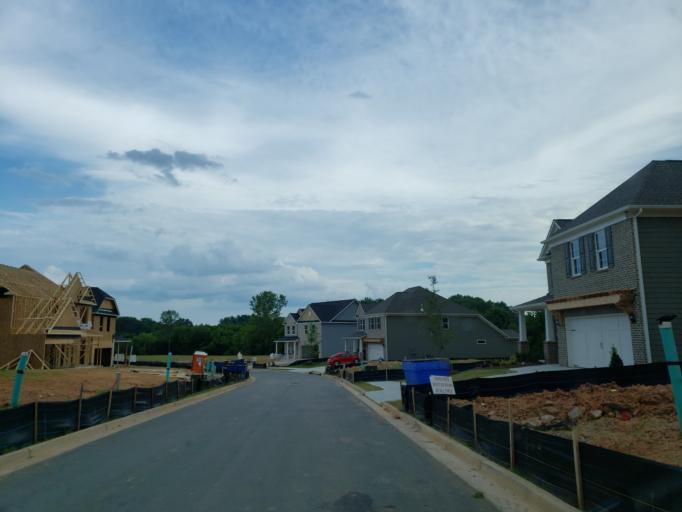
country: US
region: Georgia
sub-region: Cherokee County
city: Ball Ground
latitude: 34.2313
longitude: -84.3563
